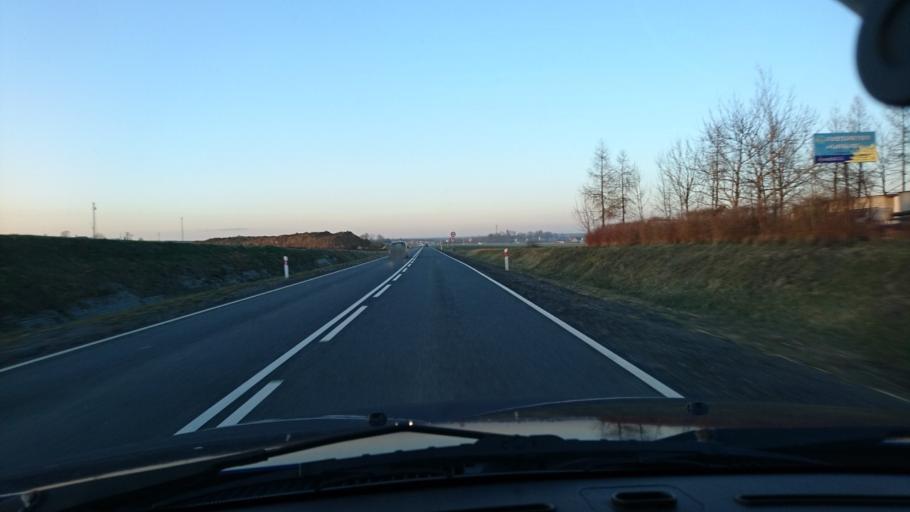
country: PL
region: Silesian Voivodeship
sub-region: Powiat gliwicki
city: Wielowies
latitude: 50.4948
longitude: 18.6073
